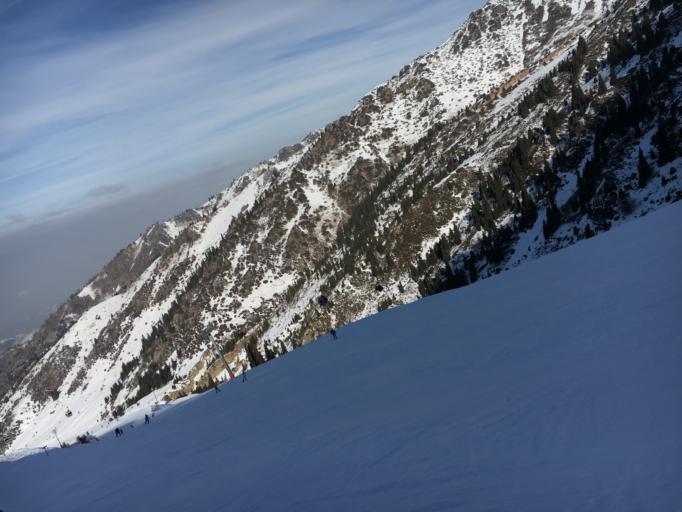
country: KZ
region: Almaty Qalasy
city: Almaty
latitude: 43.1197
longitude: 77.0964
